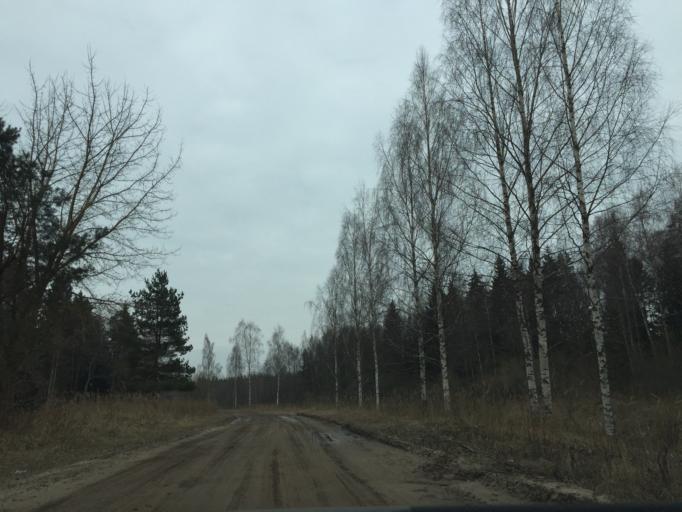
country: LV
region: Kekava
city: Balozi
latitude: 56.7811
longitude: 24.1234
